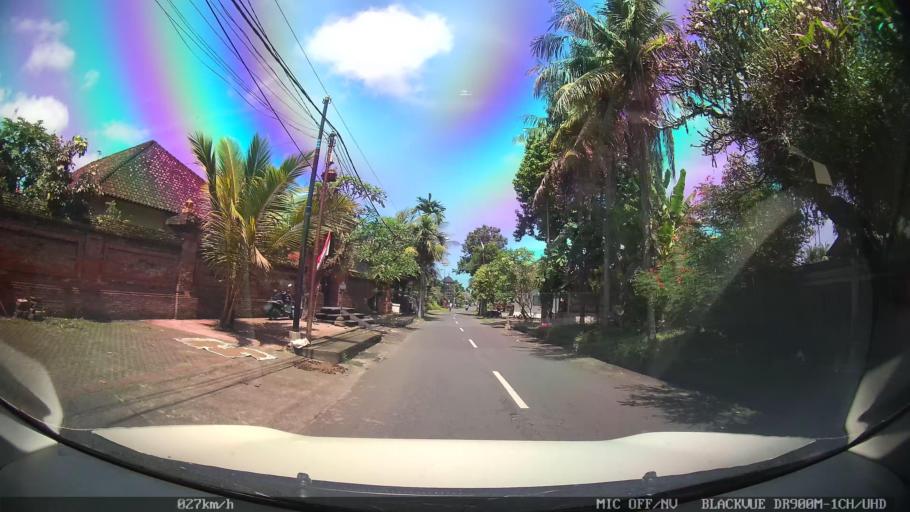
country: ID
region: Bali
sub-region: Kabupaten Gianyar
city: Ubud
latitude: -8.5557
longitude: 115.3160
